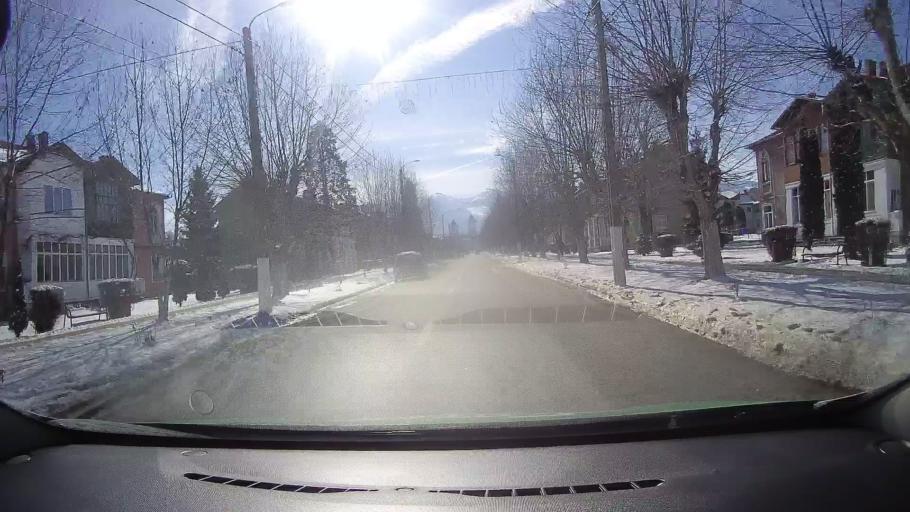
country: RO
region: Brasov
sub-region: Oras Victoria
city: Victoria
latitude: 45.7285
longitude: 24.7014
